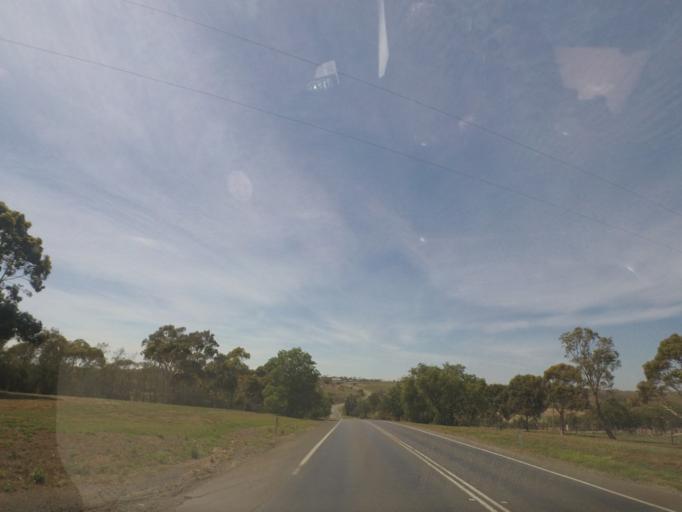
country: AU
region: Victoria
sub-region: Moorabool
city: Bacchus Marsh
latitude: -37.6951
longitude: 144.4457
